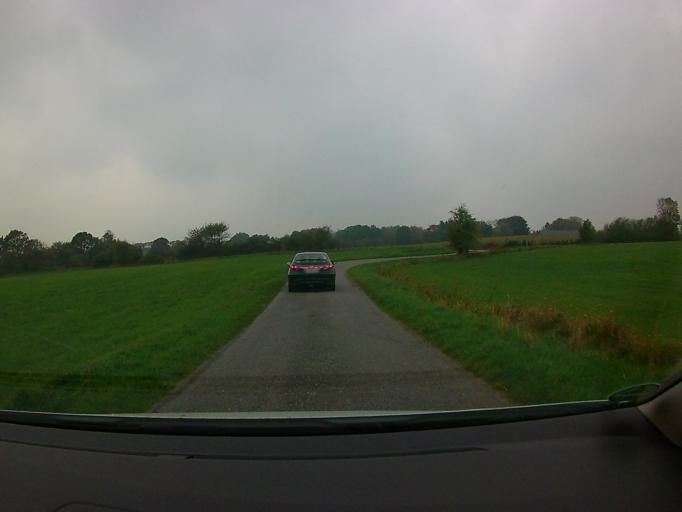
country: DE
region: Schleswig-Holstein
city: Wees
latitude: 54.8619
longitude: 9.4679
